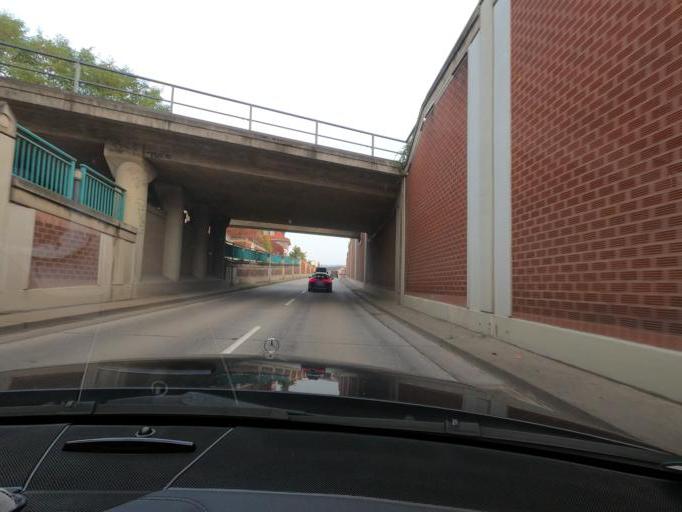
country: DE
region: Lower Saxony
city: Northeim
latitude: 51.7079
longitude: 9.9925
